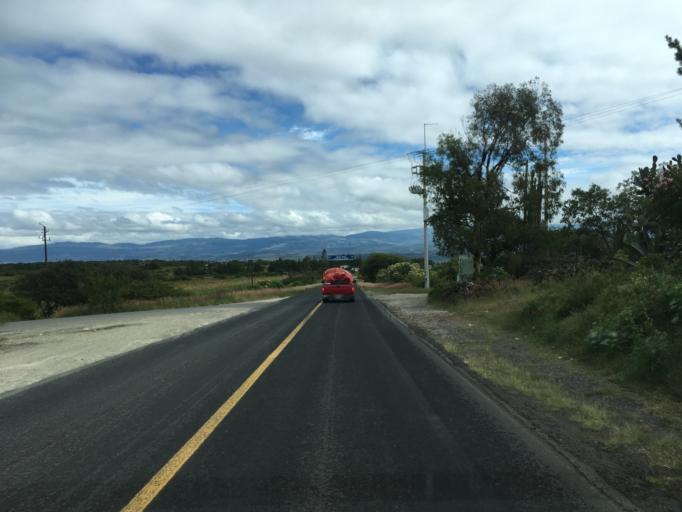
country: MX
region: Hidalgo
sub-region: Atotonilco el Grande
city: Santa Maria Amajac
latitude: 20.4109
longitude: -98.7033
